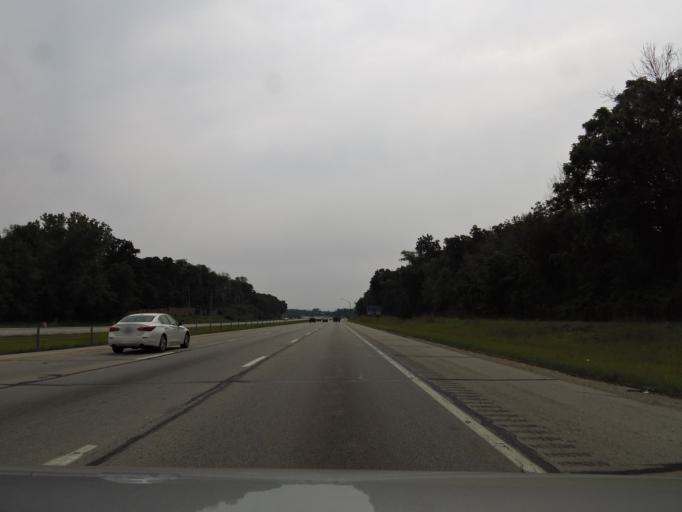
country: US
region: Ohio
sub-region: Montgomery County
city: Centerville
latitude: 39.6545
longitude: -84.1201
